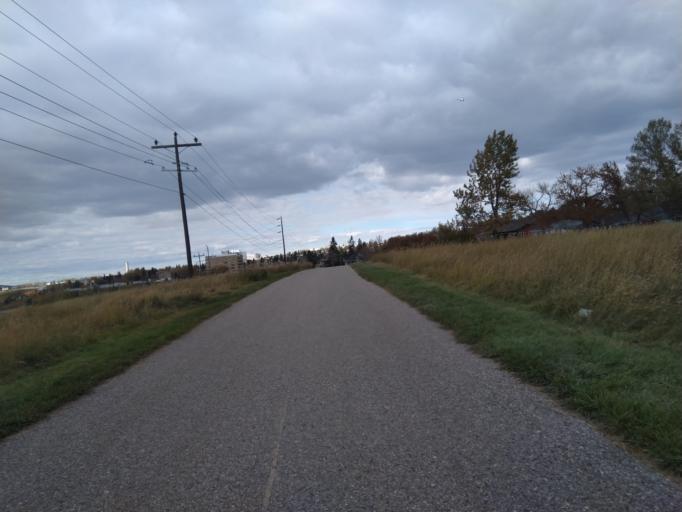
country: CA
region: Alberta
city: Calgary
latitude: 51.0324
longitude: -113.9950
